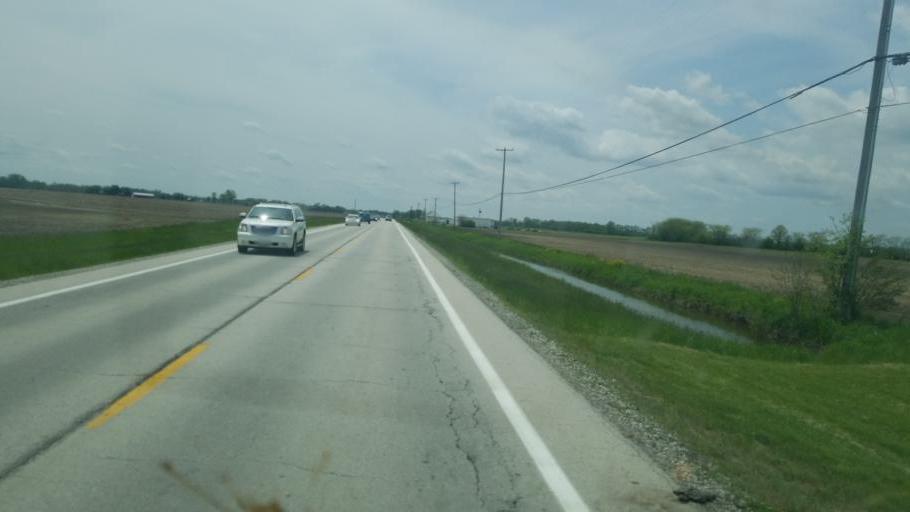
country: US
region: Ohio
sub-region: Ottawa County
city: Oak Harbor
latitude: 41.4410
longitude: -83.0648
